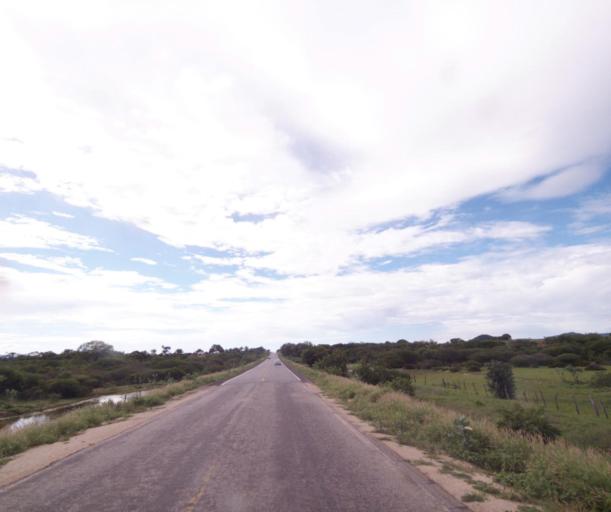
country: BR
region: Bahia
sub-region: Guanambi
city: Guanambi
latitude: -14.4093
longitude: -42.7409
